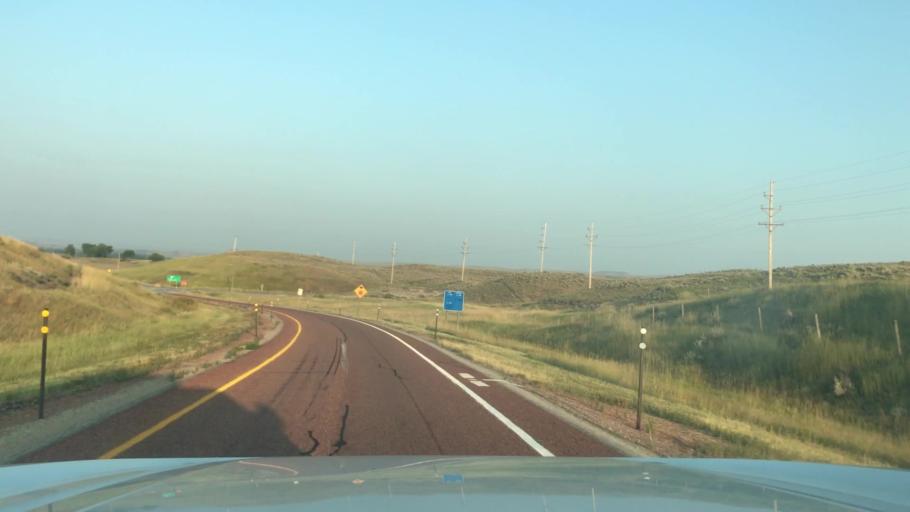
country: US
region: Wyoming
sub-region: Sheridan County
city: Sheridan
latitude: 44.9150
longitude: -107.1553
